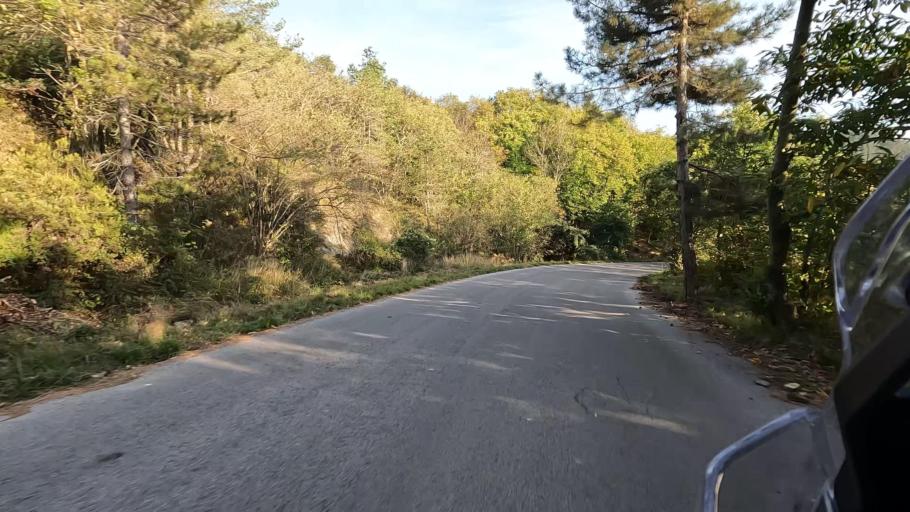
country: IT
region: Liguria
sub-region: Provincia di Savona
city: San Giovanni
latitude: 44.4199
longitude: 8.5291
